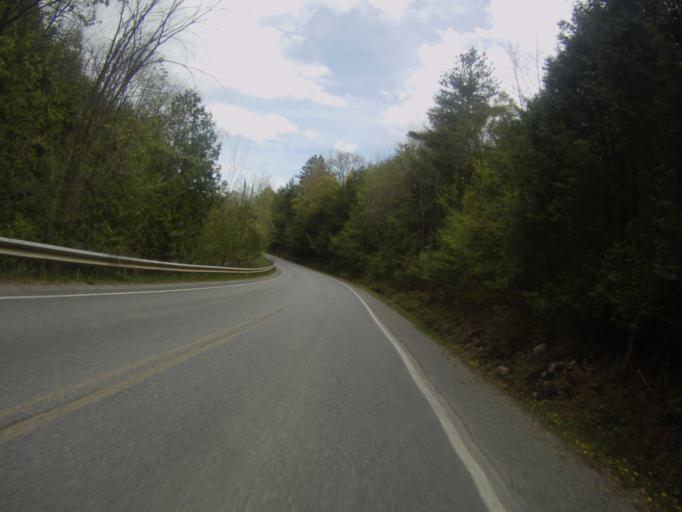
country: US
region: New York
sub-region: Essex County
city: Port Henry
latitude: 43.9462
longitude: -73.4955
